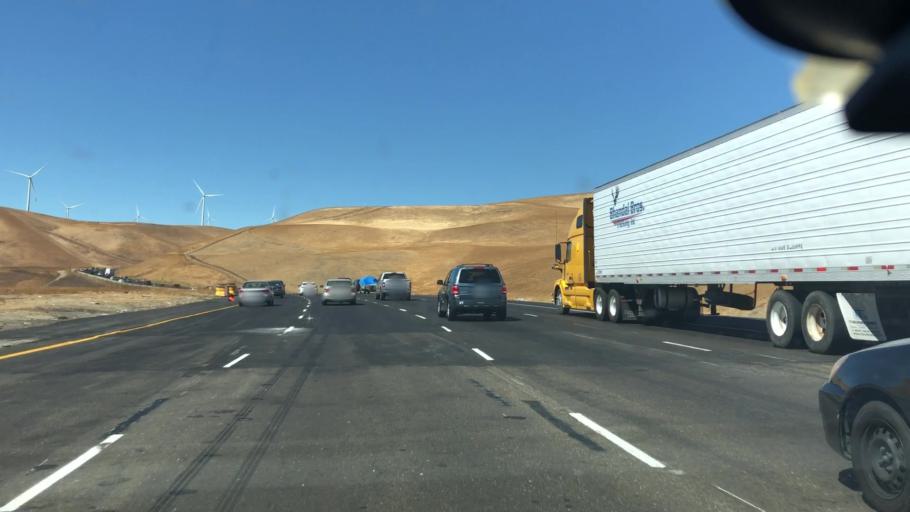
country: US
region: California
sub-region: San Joaquin County
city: Mountain House
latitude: 37.7334
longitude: -121.6312
